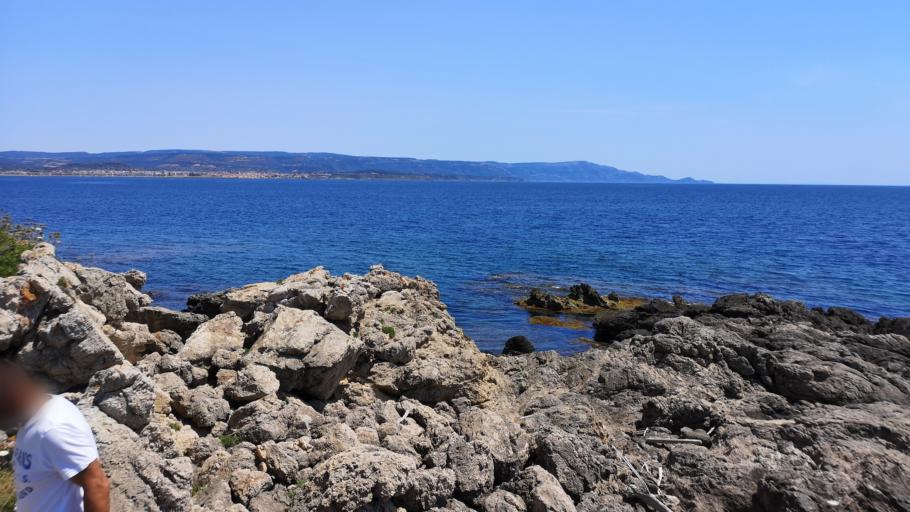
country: IT
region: Sardinia
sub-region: Provincia di Sassari
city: Alghero
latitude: 40.5814
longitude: 8.2652
